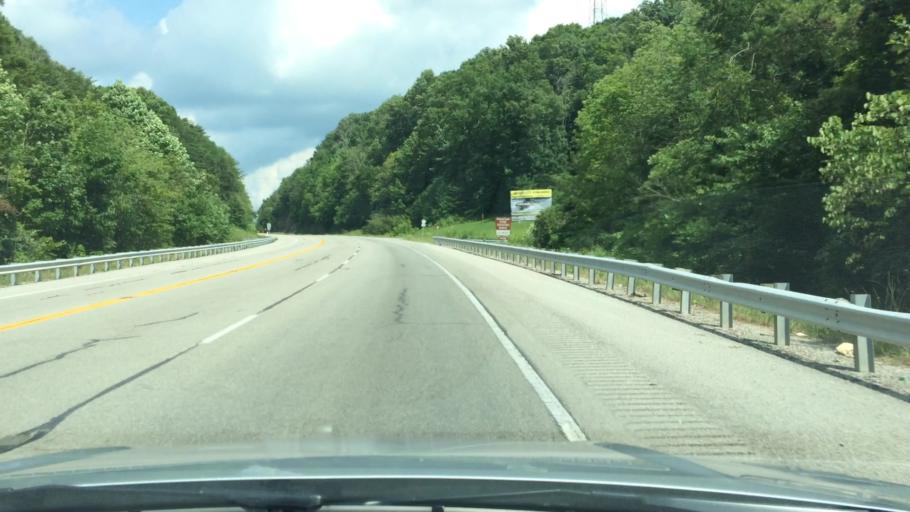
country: US
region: Kentucky
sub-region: Pulaski County
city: Somerset
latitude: 36.9469
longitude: -84.5710
